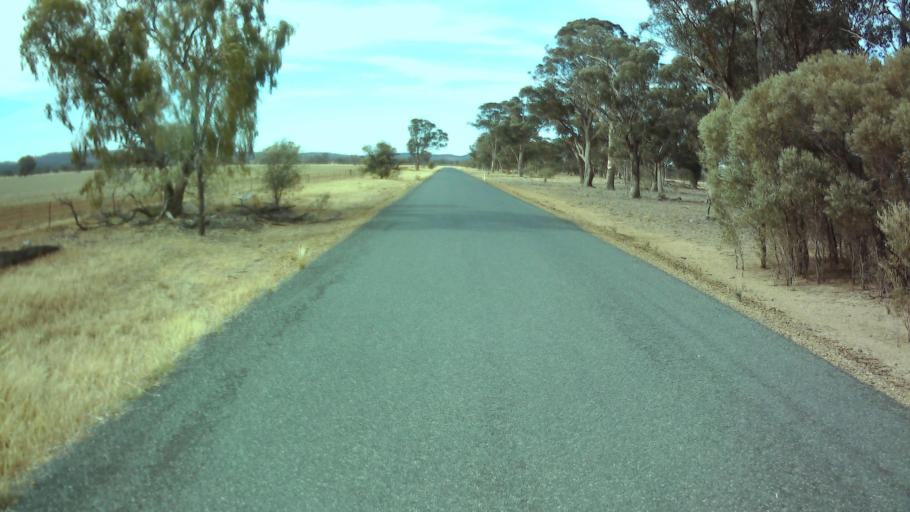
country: AU
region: New South Wales
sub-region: Weddin
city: Grenfell
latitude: -33.8611
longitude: 147.8599
